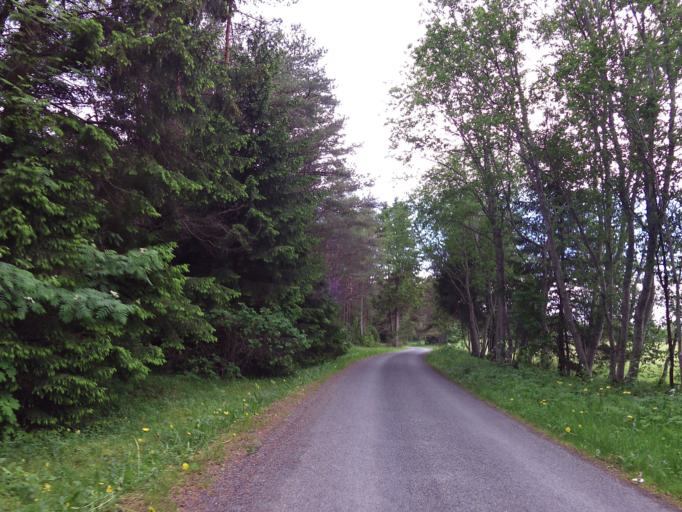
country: EE
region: Harju
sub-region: Paldiski linn
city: Paldiski
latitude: 59.2526
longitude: 23.7562
